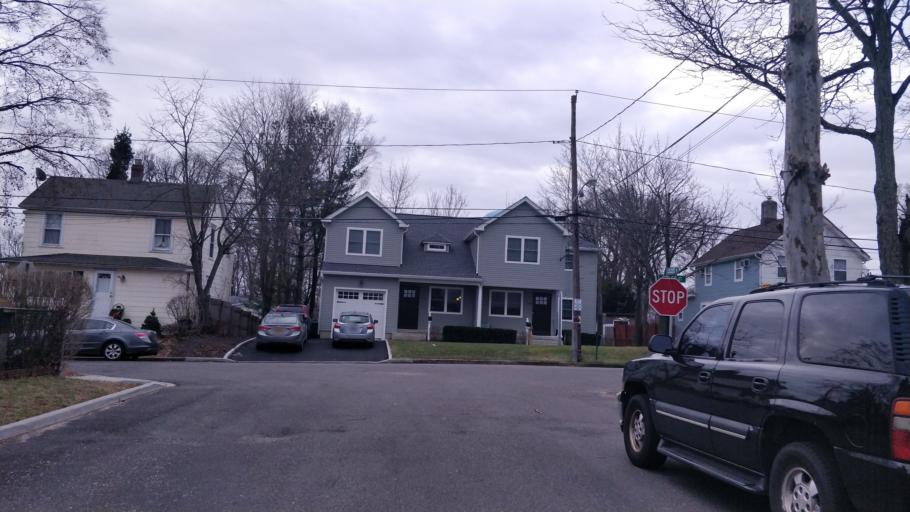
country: US
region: New York
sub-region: Nassau County
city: Glen Cove
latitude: 40.8650
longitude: -73.6442
